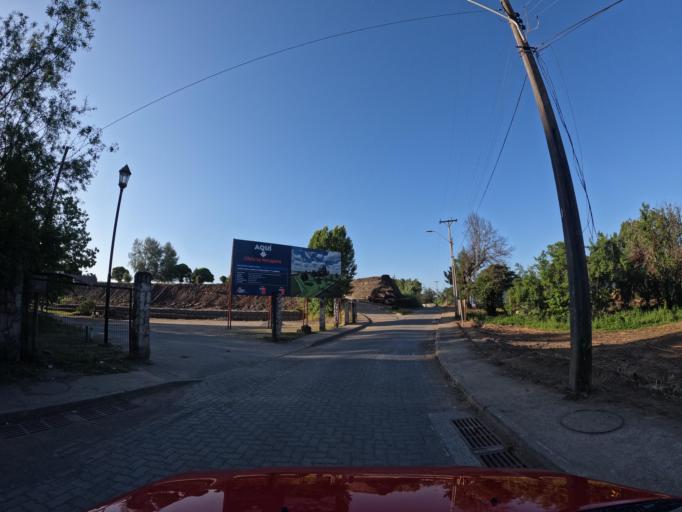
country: CL
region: Biobio
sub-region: Provincia de Concepcion
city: Lota
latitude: -37.1699
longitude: -72.9405
